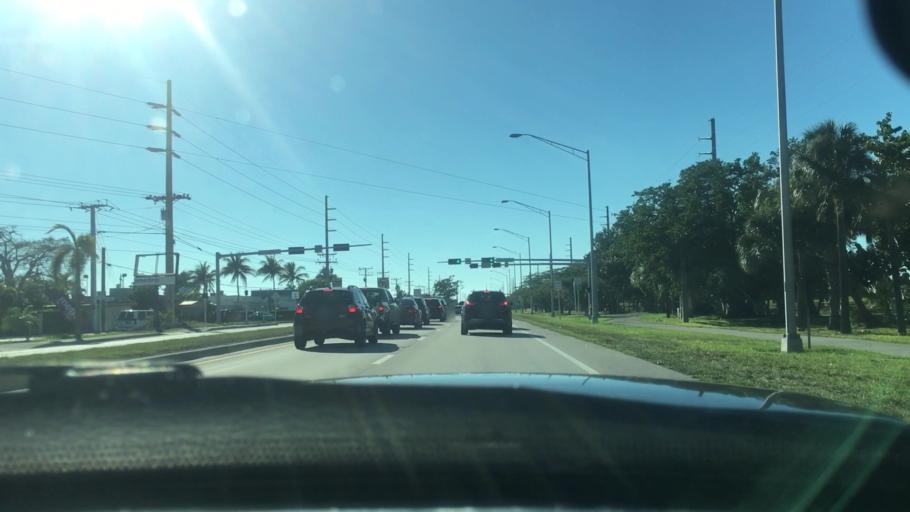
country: US
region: Florida
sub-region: Monroe County
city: Stock Island
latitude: 24.5732
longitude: -81.7419
